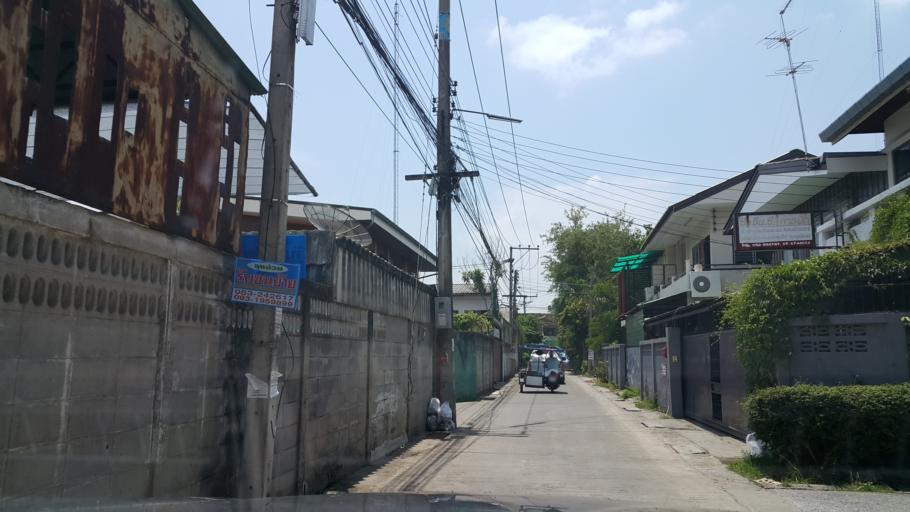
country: TH
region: Chiang Mai
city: Chiang Mai
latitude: 18.8045
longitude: 99.0021
